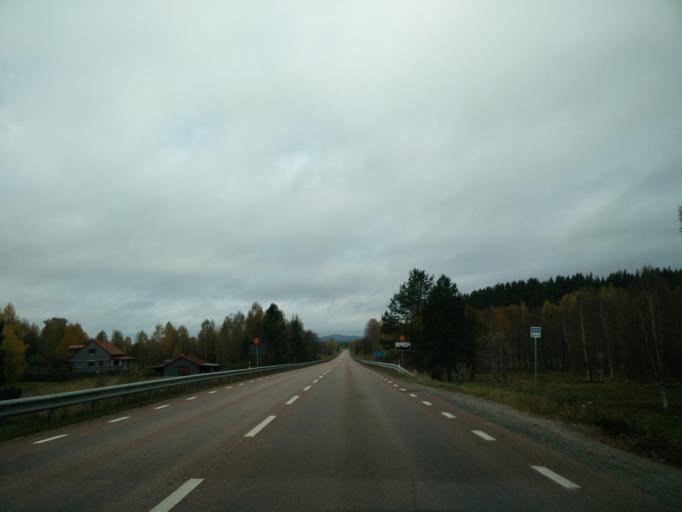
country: SE
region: Vaesternorrland
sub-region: Ange Kommun
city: Ange
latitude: 62.5192
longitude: 15.6470
